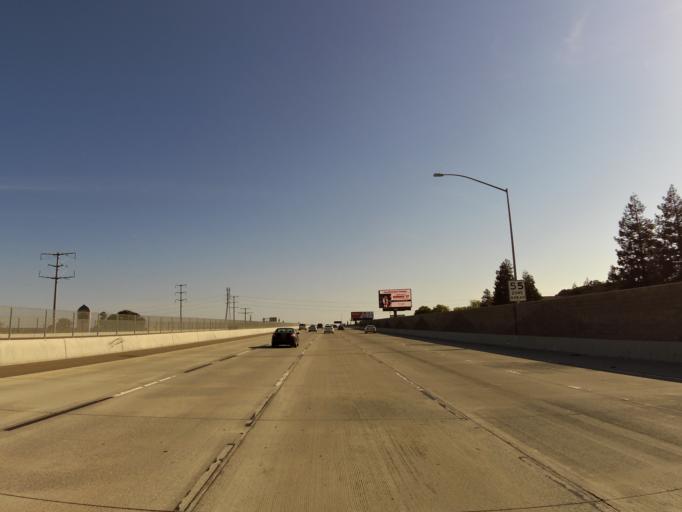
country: US
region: California
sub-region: Contra Costa County
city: Pittsburg
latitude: 38.0098
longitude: -121.8597
